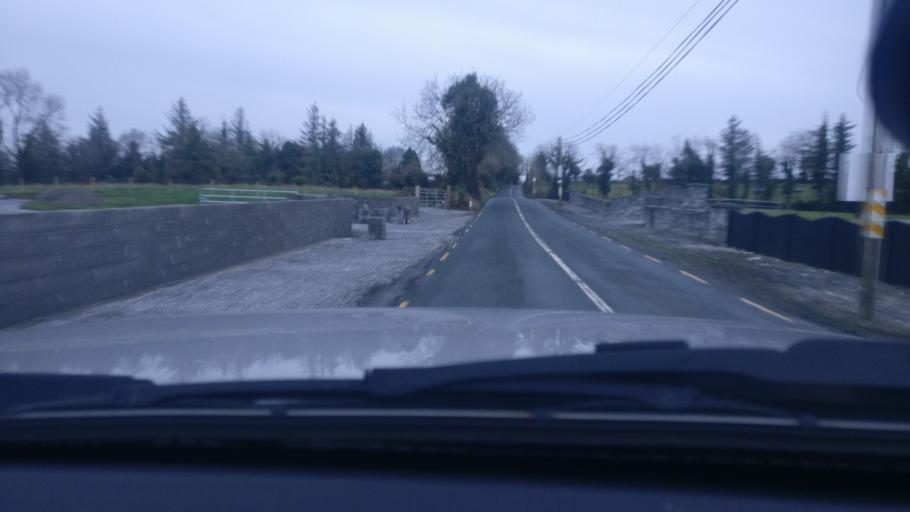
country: IE
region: Connaught
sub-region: County Galway
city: Loughrea
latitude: 53.1681
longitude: -8.5221
